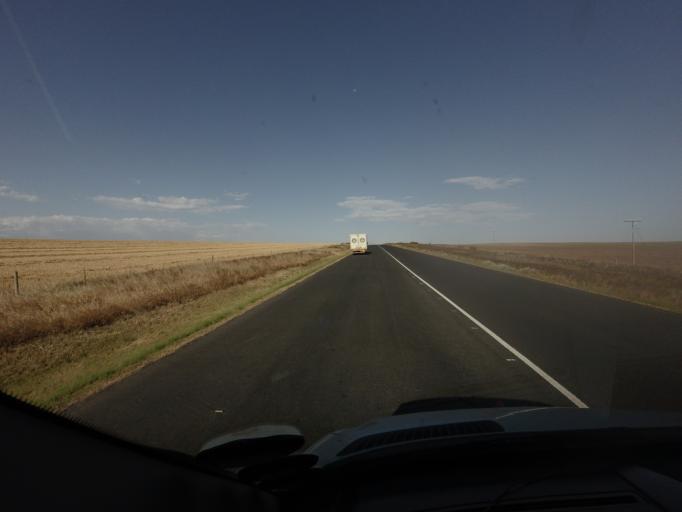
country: ZA
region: Western Cape
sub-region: Cape Winelands District Municipality
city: Ashton
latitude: -34.1409
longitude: 20.0151
